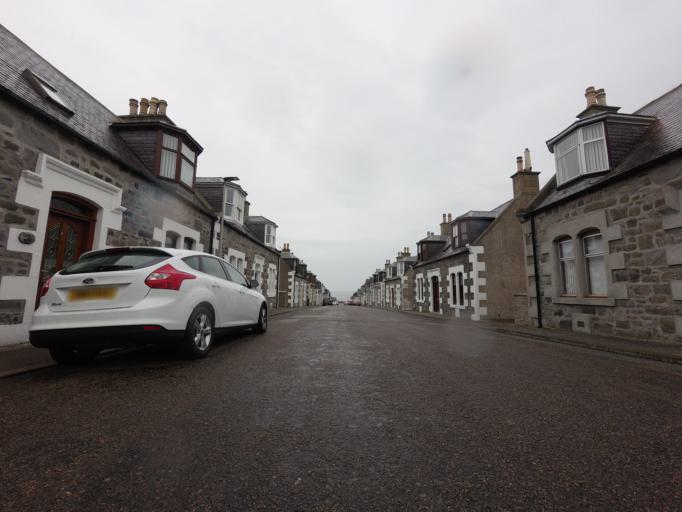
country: GB
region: Scotland
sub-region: Moray
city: Portknockie
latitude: 57.7024
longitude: -2.8558
